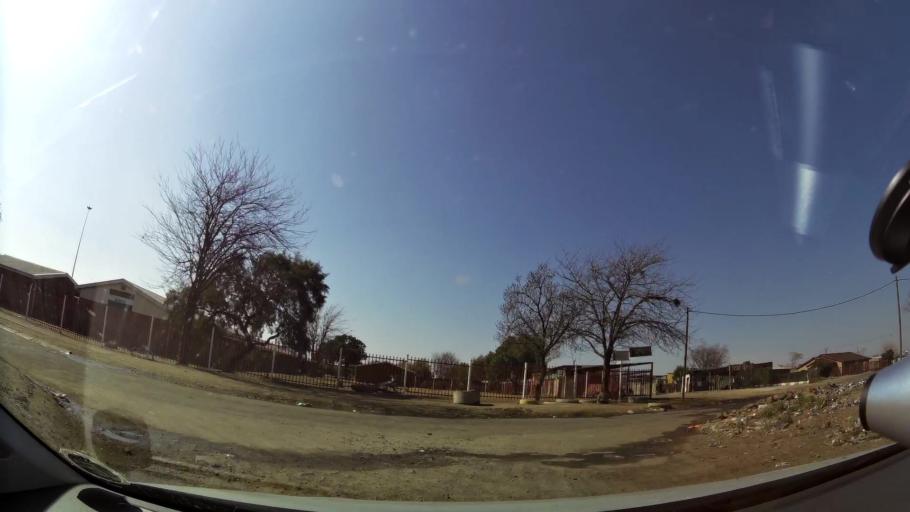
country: ZA
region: Orange Free State
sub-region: Mangaung Metropolitan Municipality
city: Bloemfontein
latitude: -29.1487
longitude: 26.2474
